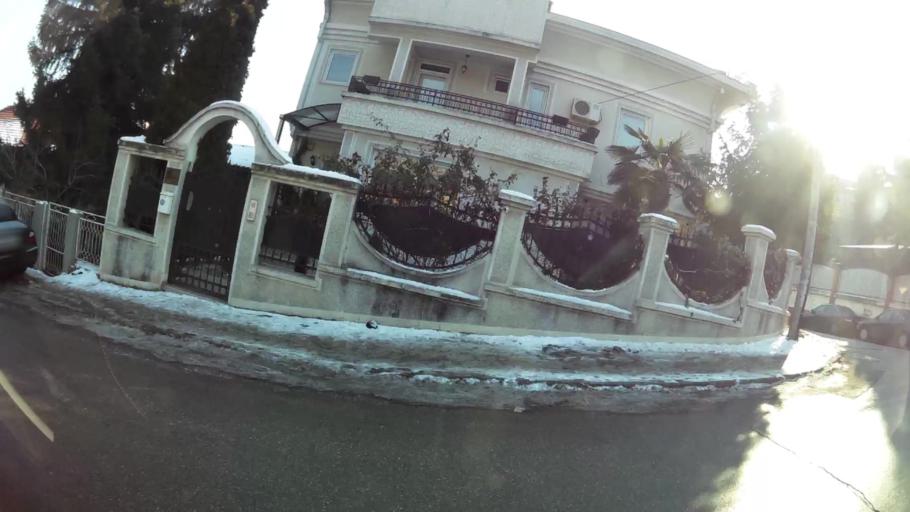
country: MK
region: Karpos
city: Skopje
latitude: 41.9760
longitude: 21.4328
